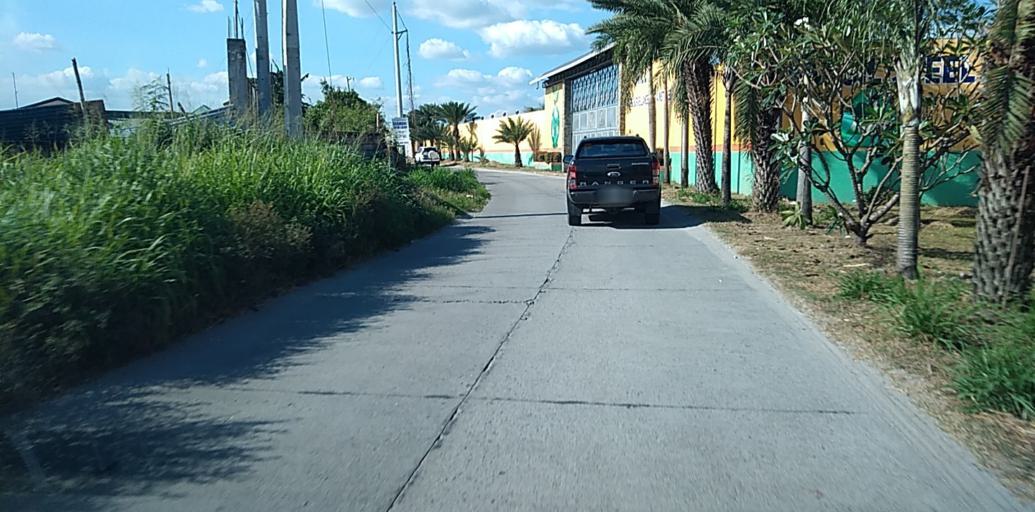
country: PH
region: Central Luzon
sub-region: Province of Pampanga
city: Acli
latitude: 15.1132
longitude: 120.6476
